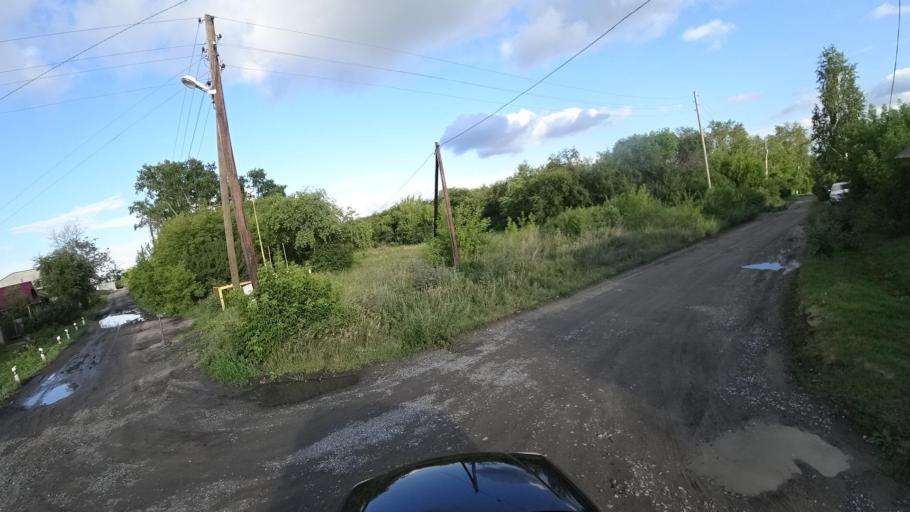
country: RU
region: Sverdlovsk
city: Kamyshlov
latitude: 56.8491
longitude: 62.6732
